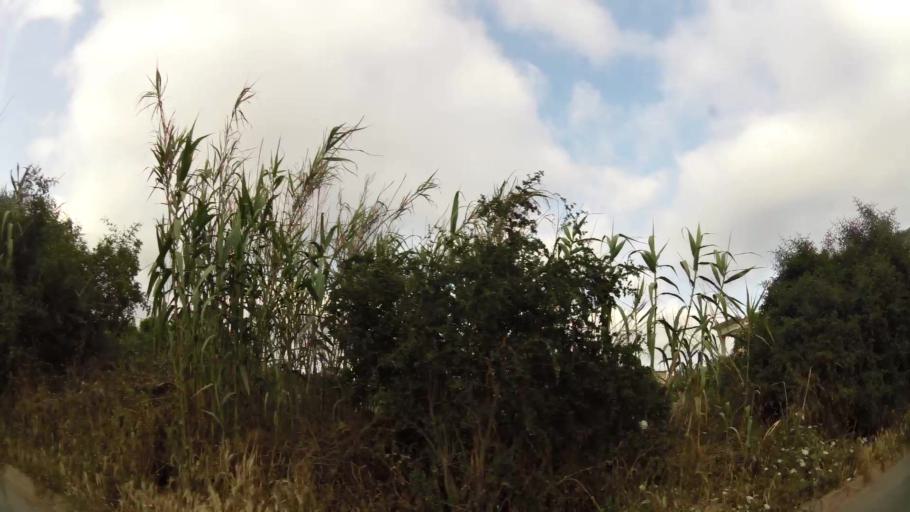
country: MA
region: Rabat-Sale-Zemmour-Zaer
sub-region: Rabat
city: Rabat
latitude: 33.9505
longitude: -6.8447
